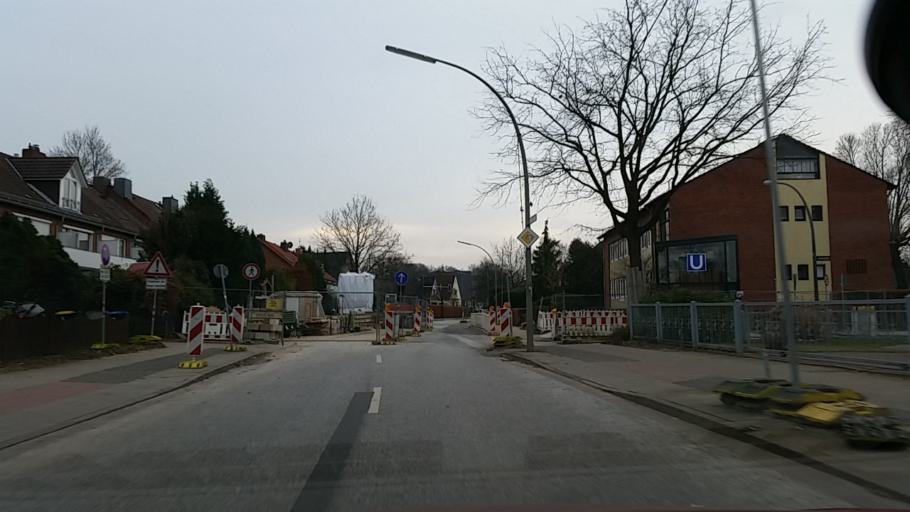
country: DE
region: Hamburg
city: Stellingen
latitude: 53.6283
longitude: 9.9502
